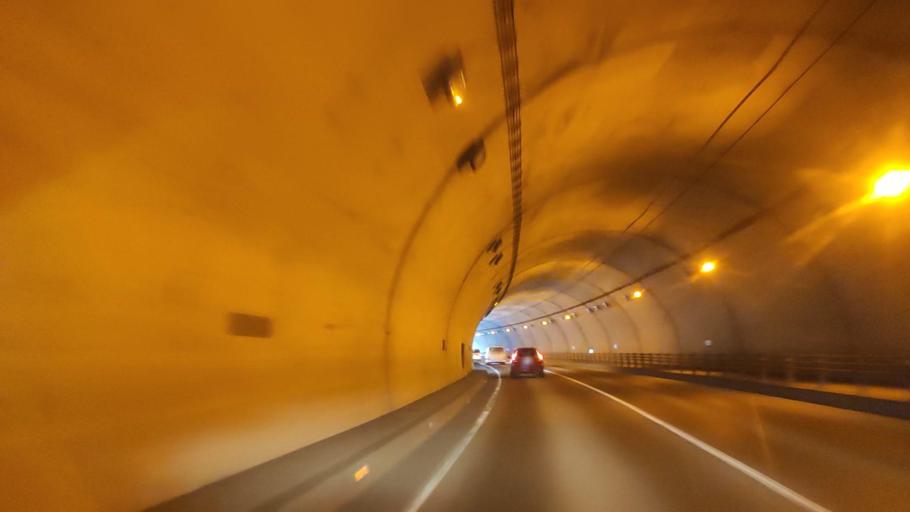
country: JP
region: Hokkaido
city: Iwamizawa
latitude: 43.0289
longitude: 141.9606
